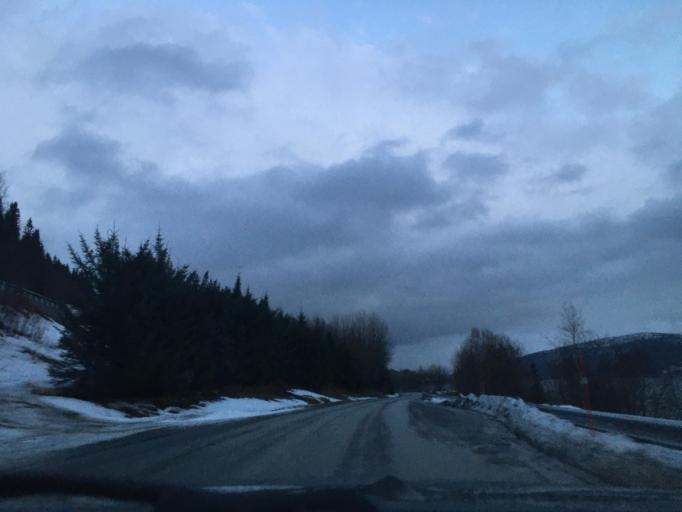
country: NO
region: Nordland
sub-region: Rana
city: Hauknes
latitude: 66.3075
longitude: 13.9762
